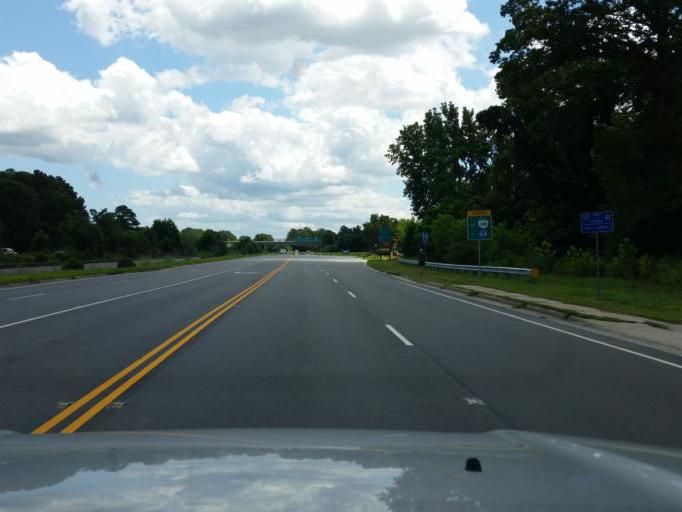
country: US
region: Virginia
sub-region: City of Williamsburg
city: Williamsburg
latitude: 37.2554
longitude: -76.6675
